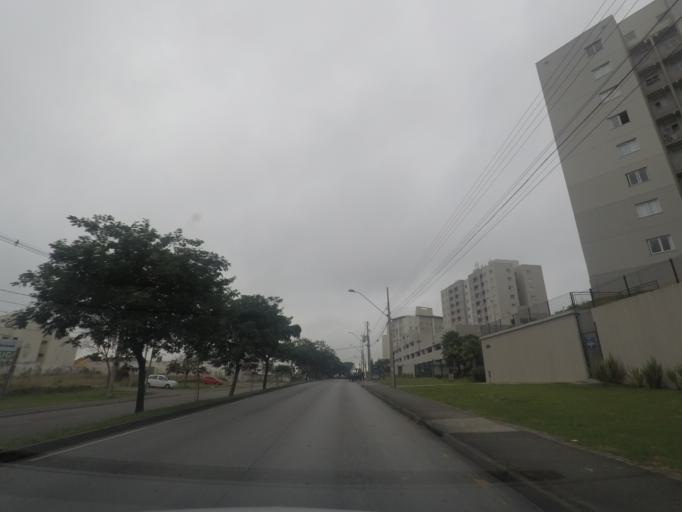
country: BR
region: Parana
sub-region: Pinhais
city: Pinhais
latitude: -25.3855
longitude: -49.2137
